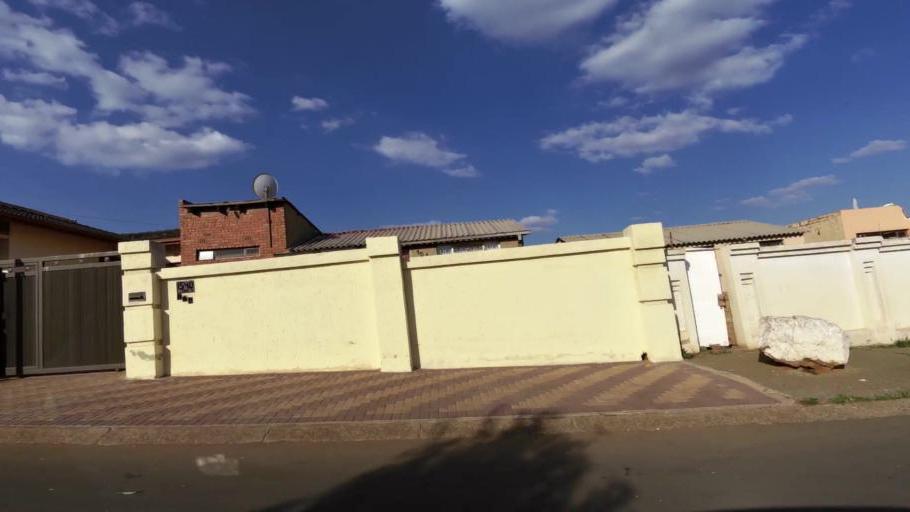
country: ZA
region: Gauteng
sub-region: City of Johannesburg Metropolitan Municipality
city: Roodepoort
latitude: -26.2035
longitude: 27.8788
